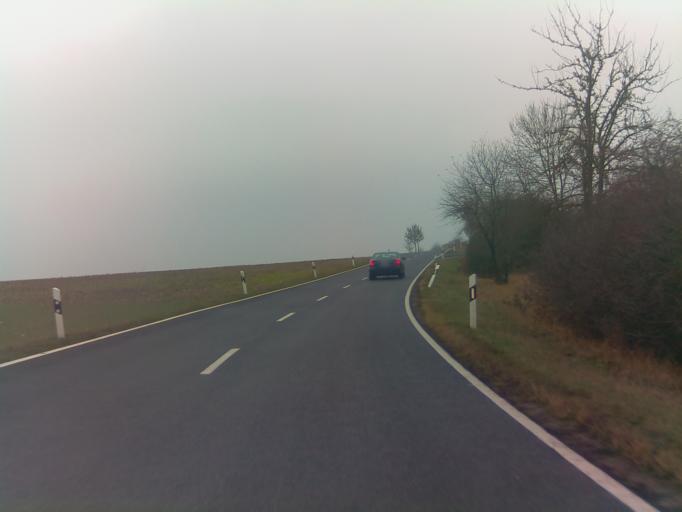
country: DE
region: Thuringia
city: Leutersdorf
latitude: 50.4867
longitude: 10.5675
